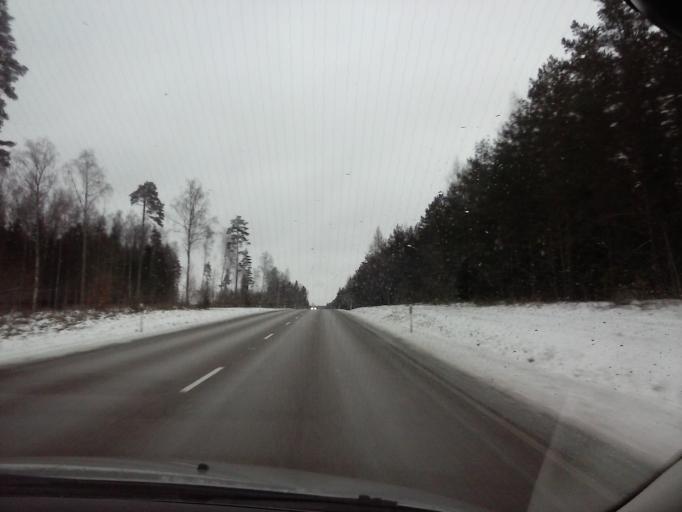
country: EE
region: Valgamaa
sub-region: Torva linn
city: Torva
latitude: 58.0591
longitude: 26.1964
